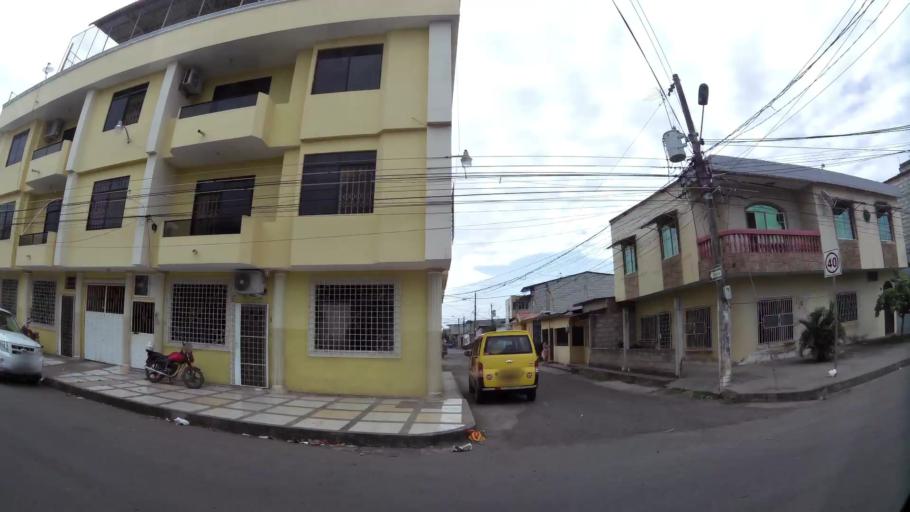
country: EC
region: El Oro
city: Machala
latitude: -3.2485
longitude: -79.9490
